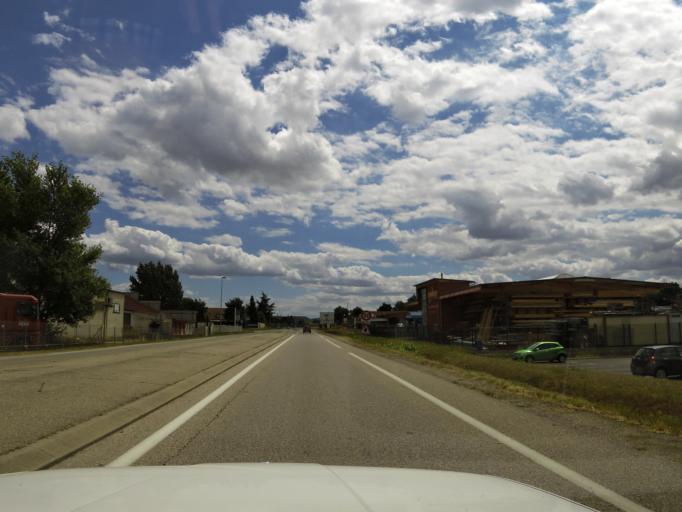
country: FR
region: Rhone-Alpes
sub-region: Departement de l'Isere
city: Saint-Romain-de-Jalionas
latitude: 45.7638
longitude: 5.2075
